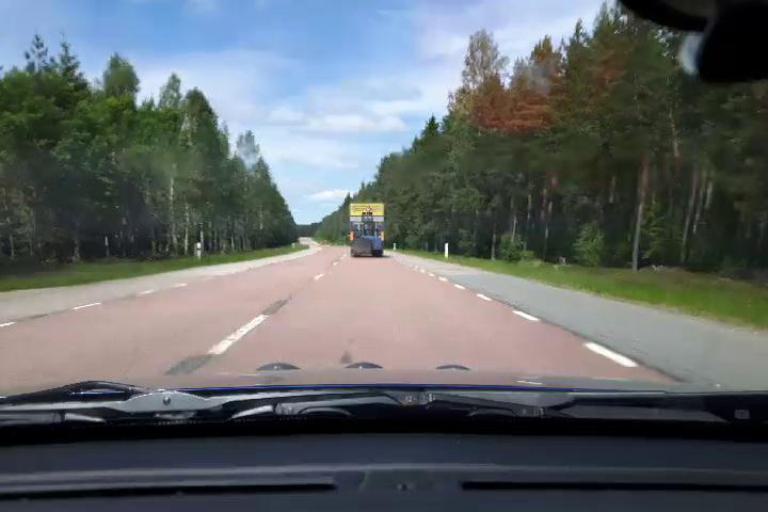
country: SE
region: Uppsala
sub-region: Osthammars Kommun
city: Bjorklinge
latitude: 60.1319
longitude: 17.5091
